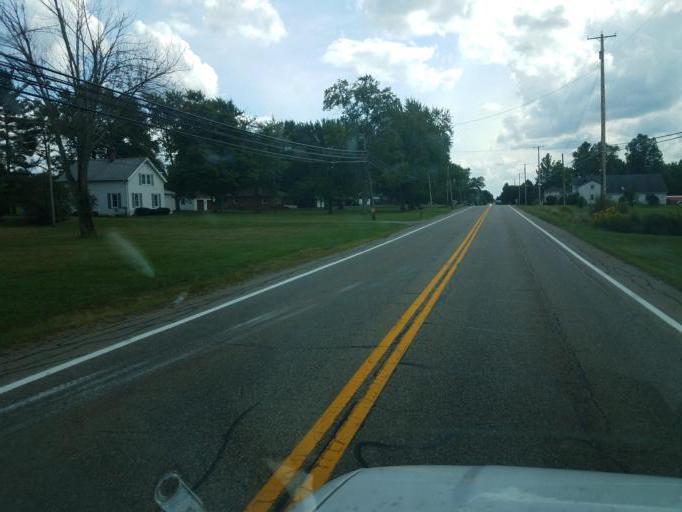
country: US
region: Ohio
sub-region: Portage County
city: Ravenna
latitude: 41.0919
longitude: -81.2428
